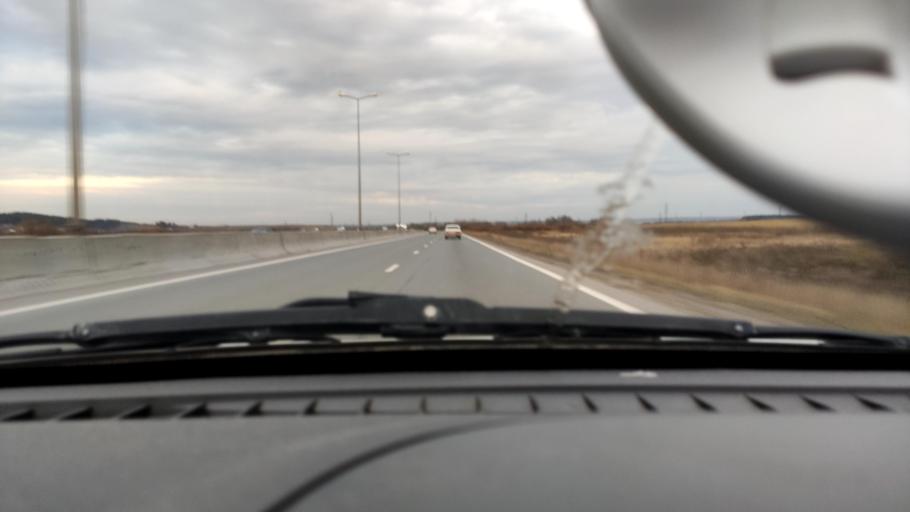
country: RU
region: Perm
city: Kondratovo
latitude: 57.9284
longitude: 56.1800
